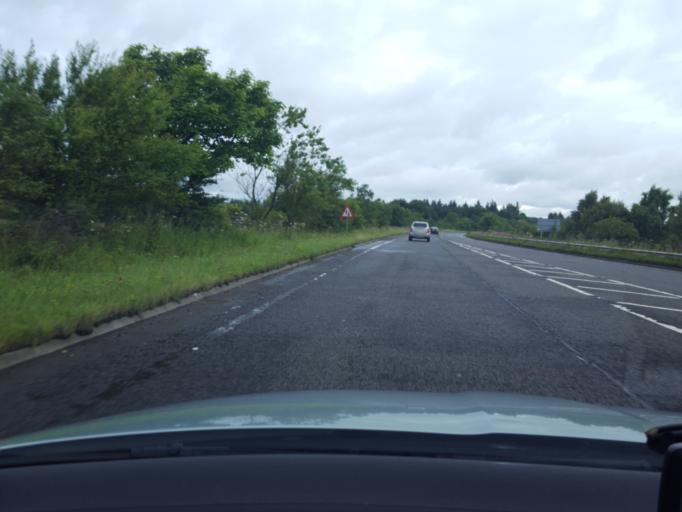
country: GB
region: Scotland
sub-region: West Lothian
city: Bathgate
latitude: 55.9224
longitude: -3.6796
